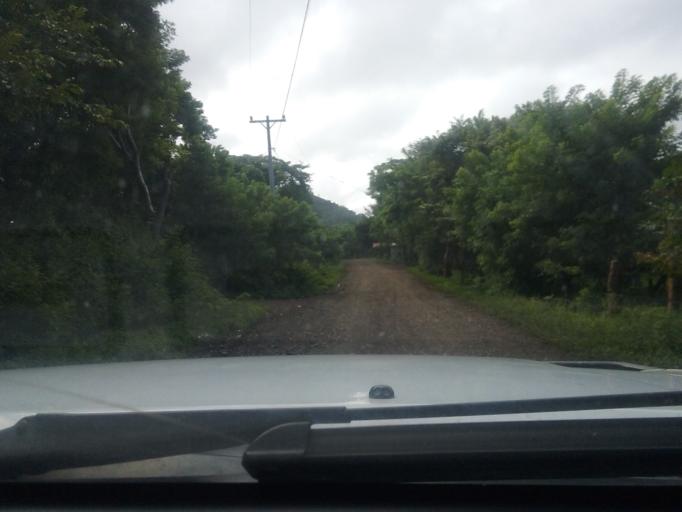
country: NI
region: Matagalpa
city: Matagalpa
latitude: 12.8818
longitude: -85.9654
